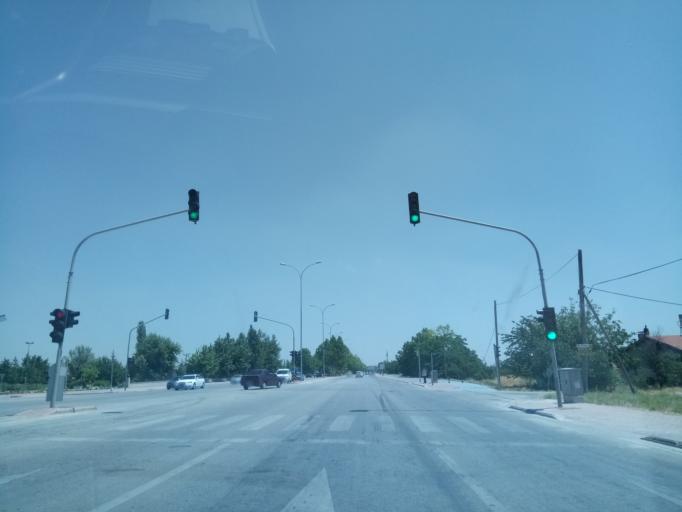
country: TR
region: Konya
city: Meram
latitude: 37.8189
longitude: 32.4553
